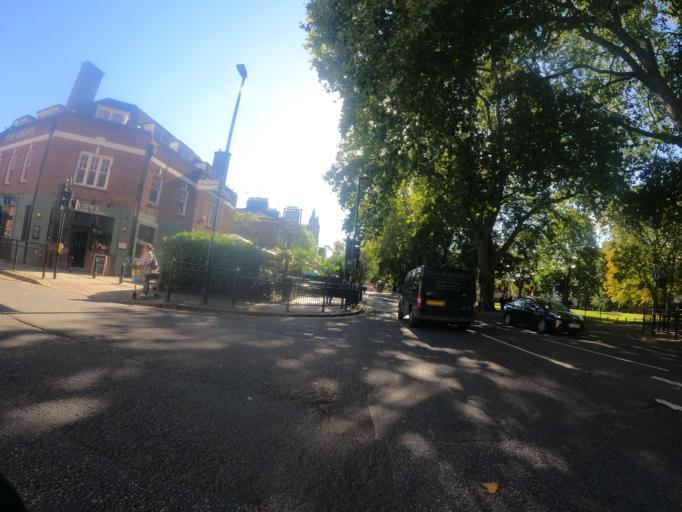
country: GB
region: England
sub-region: Greater London
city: Ealing
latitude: 51.5104
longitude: -0.3056
